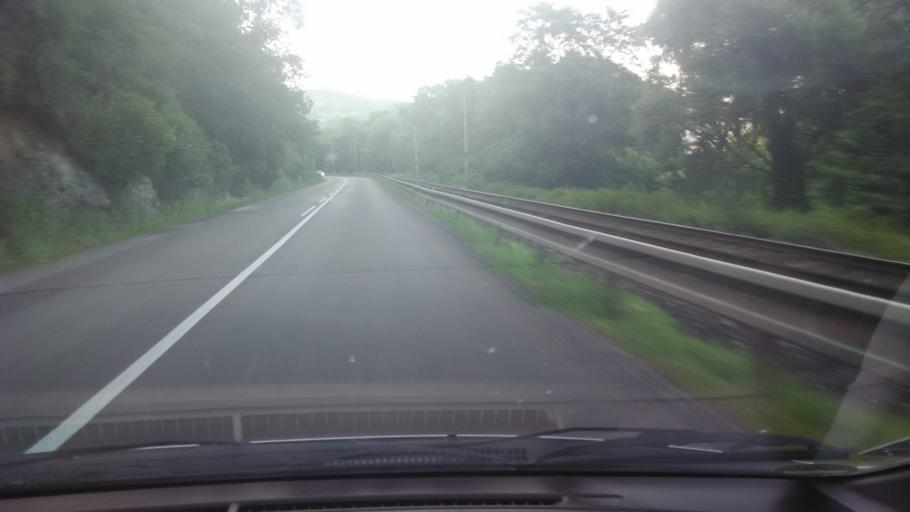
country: SK
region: Nitriansky
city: Tlmace
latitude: 48.3354
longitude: 18.5581
